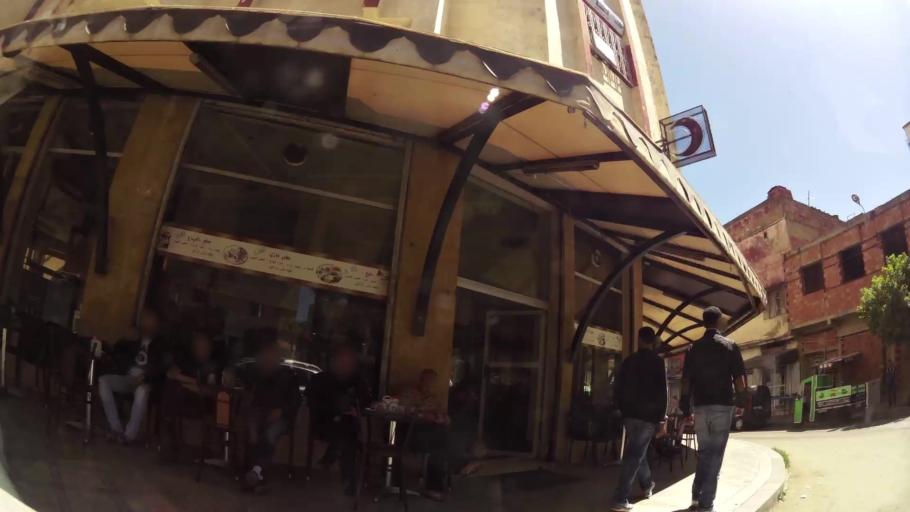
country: MA
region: Meknes-Tafilalet
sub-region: Meknes
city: Meknes
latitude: 33.9052
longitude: -5.5234
